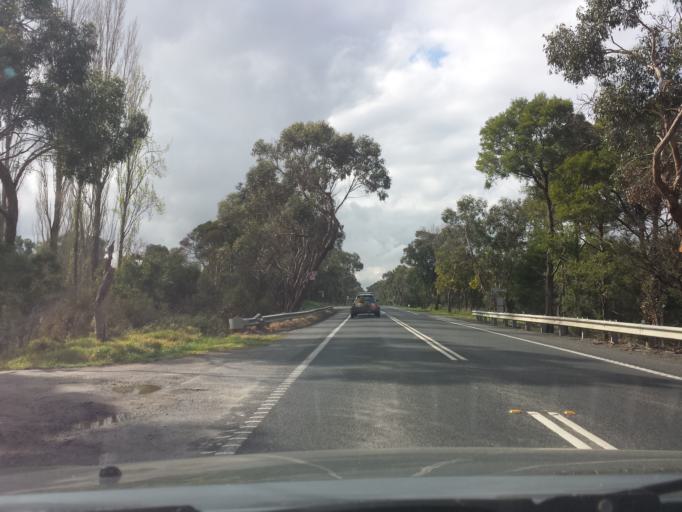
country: AU
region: Victoria
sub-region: Casey
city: Narre Warren North
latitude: -37.9654
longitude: 145.3262
